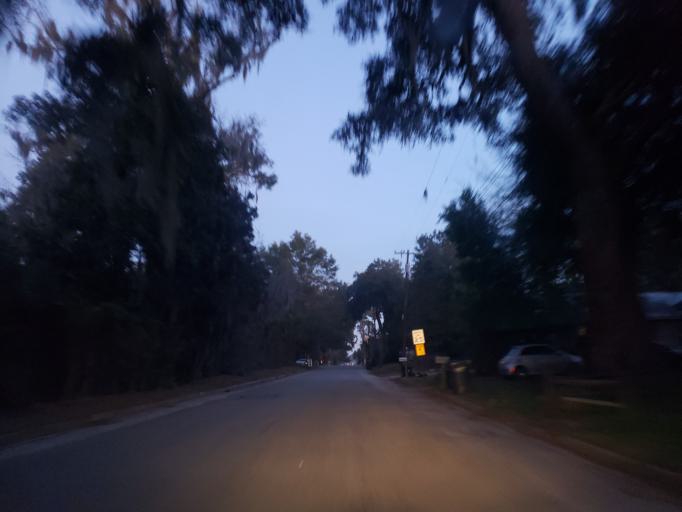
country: US
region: Georgia
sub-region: Chatham County
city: Thunderbolt
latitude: 32.0146
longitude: -81.0632
